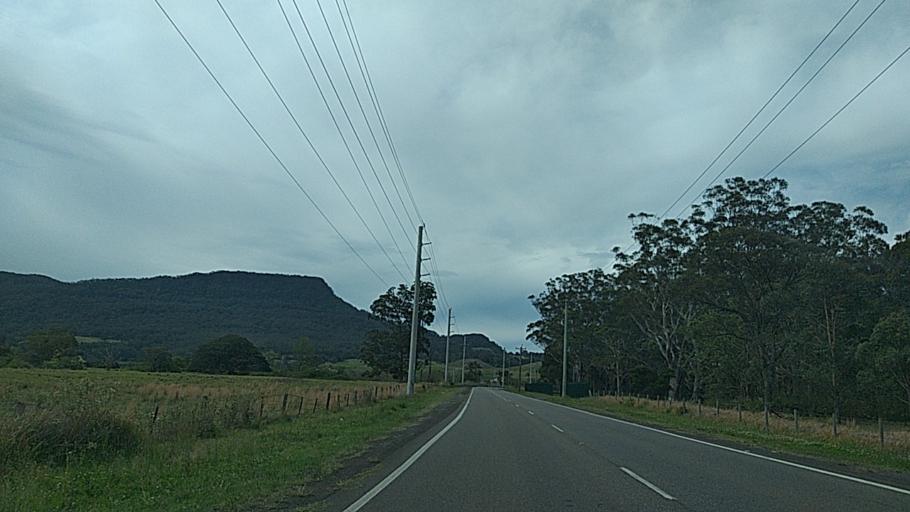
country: AU
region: New South Wales
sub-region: Wollongong
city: Dapto
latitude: -34.4723
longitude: 150.7928
